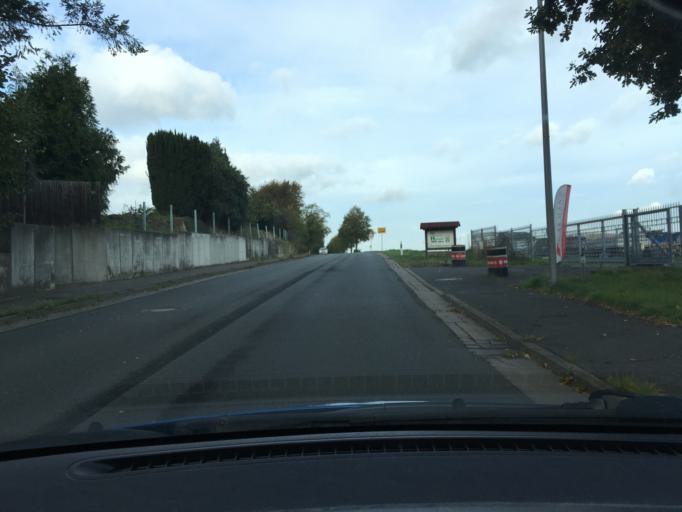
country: DE
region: Lower Saxony
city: Barsinghausen
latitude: 52.3204
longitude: 9.4278
